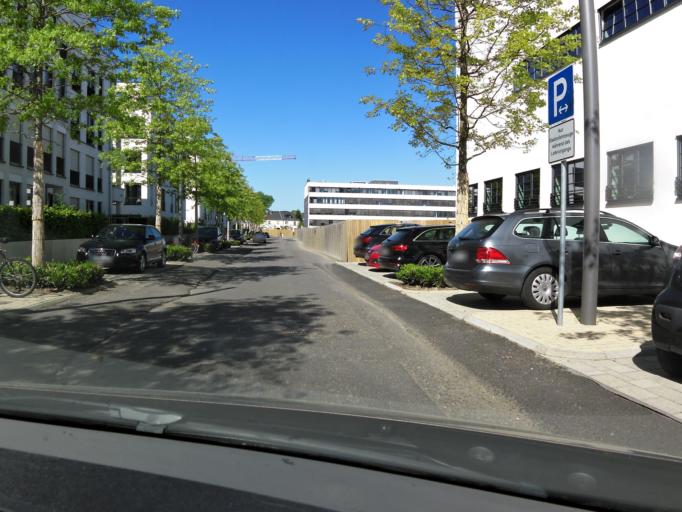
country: DE
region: North Rhine-Westphalia
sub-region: Regierungsbezirk Koln
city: Mengenich
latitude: 50.9409
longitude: 6.8885
